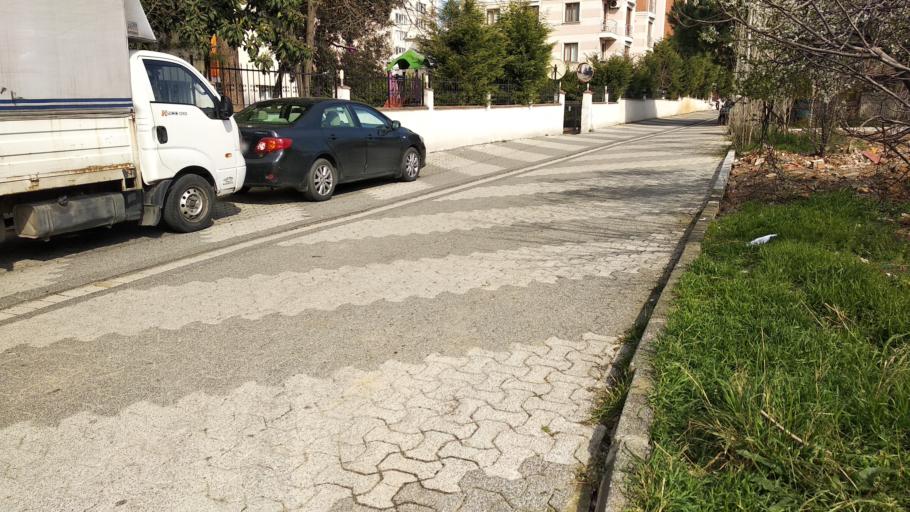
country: TR
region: Istanbul
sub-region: Atasehir
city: Atasehir
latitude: 40.9861
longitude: 29.1161
